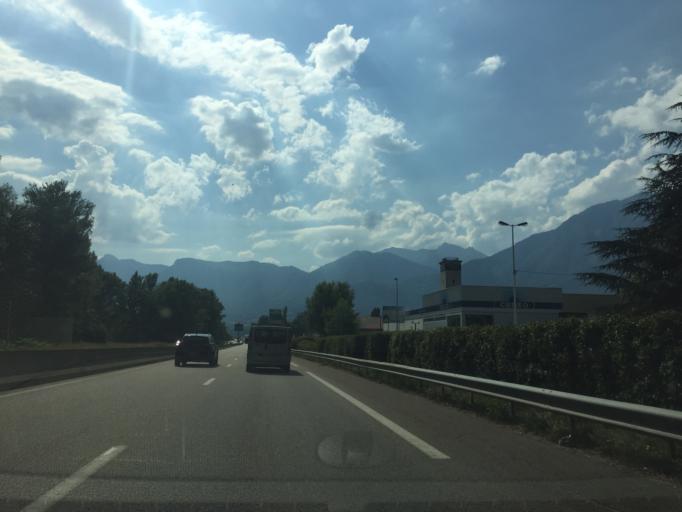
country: FR
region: Rhone-Alpes
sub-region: Departement de la Savoie
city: Albertville
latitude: 45.6632
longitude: 6.3978
